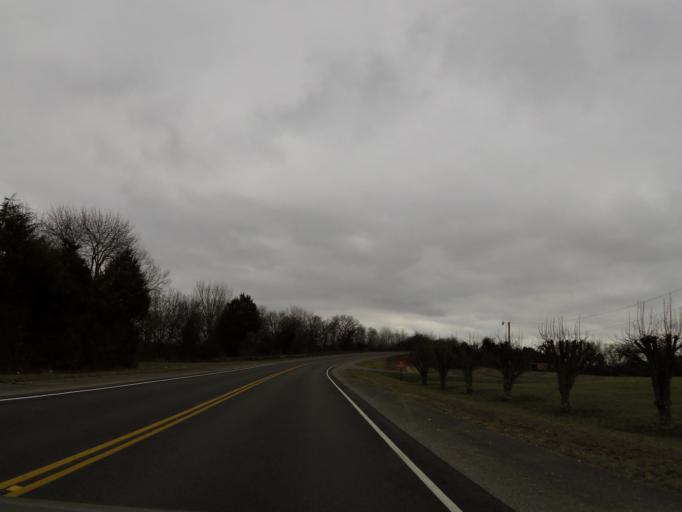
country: US
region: Tennessee
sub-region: Jefferson County
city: Jefferson City
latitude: 36.1370
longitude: -83.4714
